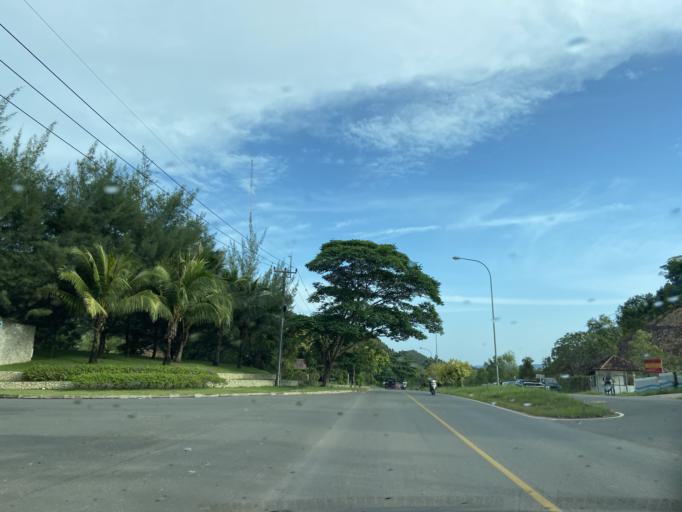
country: SG
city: Singapore
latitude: 0.9859
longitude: 104.0383
